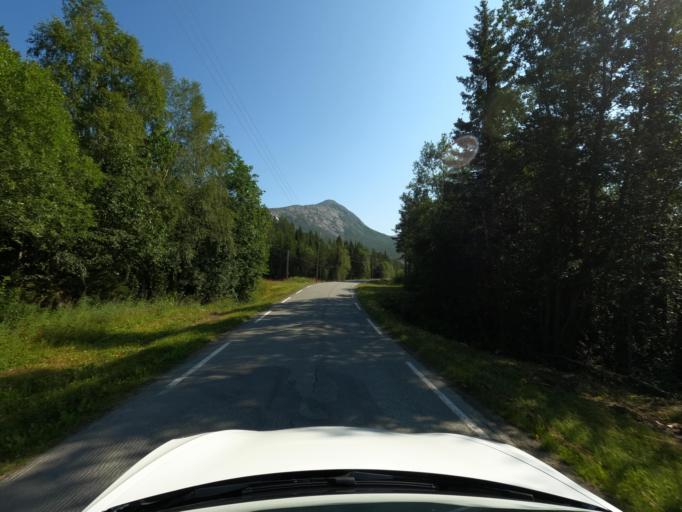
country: NO
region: Nordland
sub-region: Narvik
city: Narvik
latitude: 68.2007
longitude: 17.5470
